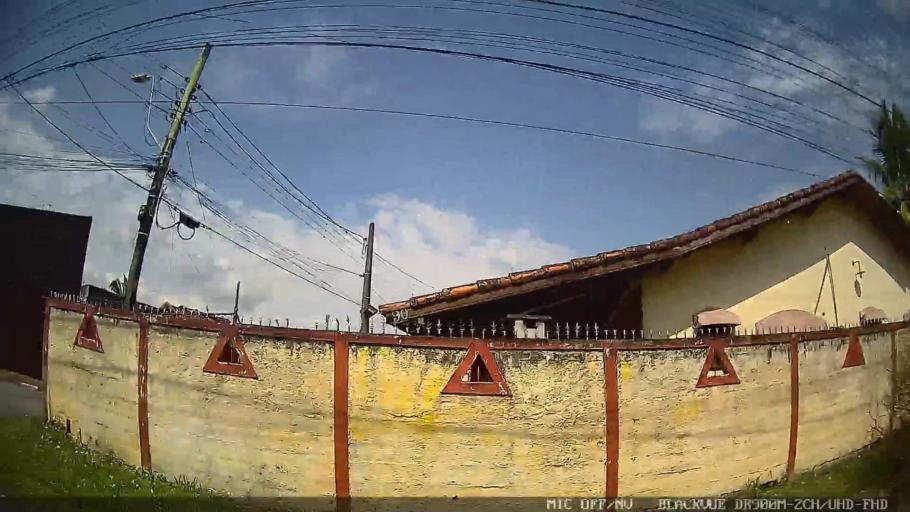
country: BR
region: Sao Paulo
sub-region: Caraguatatuba
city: Caraguatatuba
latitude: -23.6832
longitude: -45.4533
